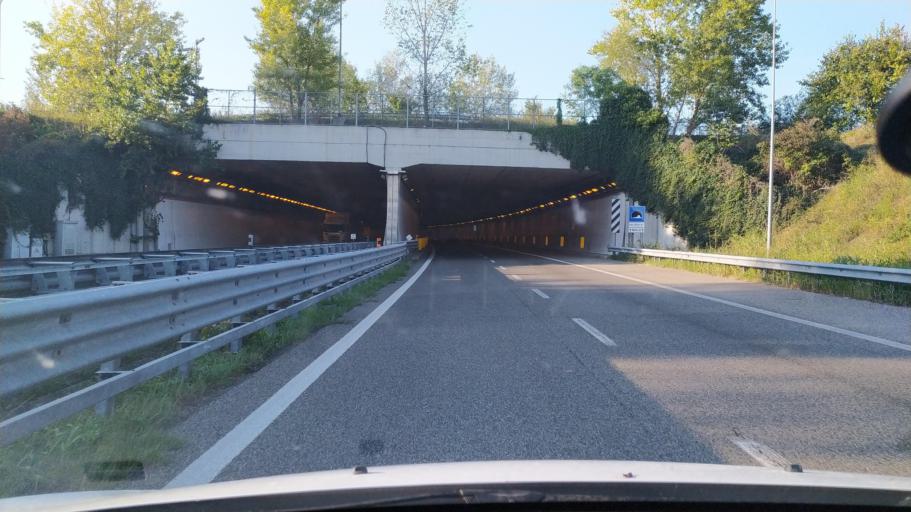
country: IT
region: Lombardy
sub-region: Citta metropolitana di Milano
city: Casate
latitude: 45.5067
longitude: 8.8308
